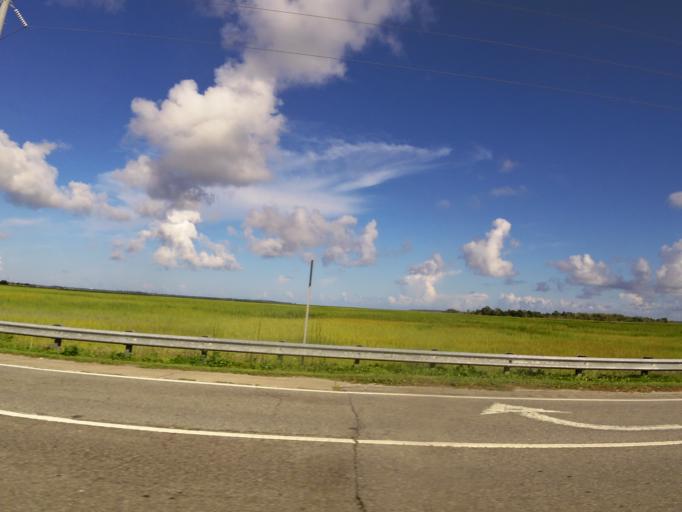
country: US
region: Georgia
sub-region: Glynn County
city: Brunswick
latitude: 31.1597
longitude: -81.4777
